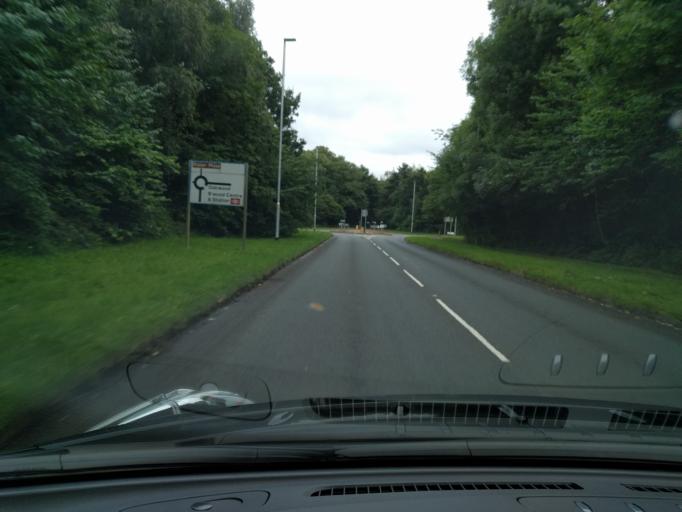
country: GB
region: England
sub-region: Warrington
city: Culcheth
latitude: 53.4260
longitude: -2.5070
